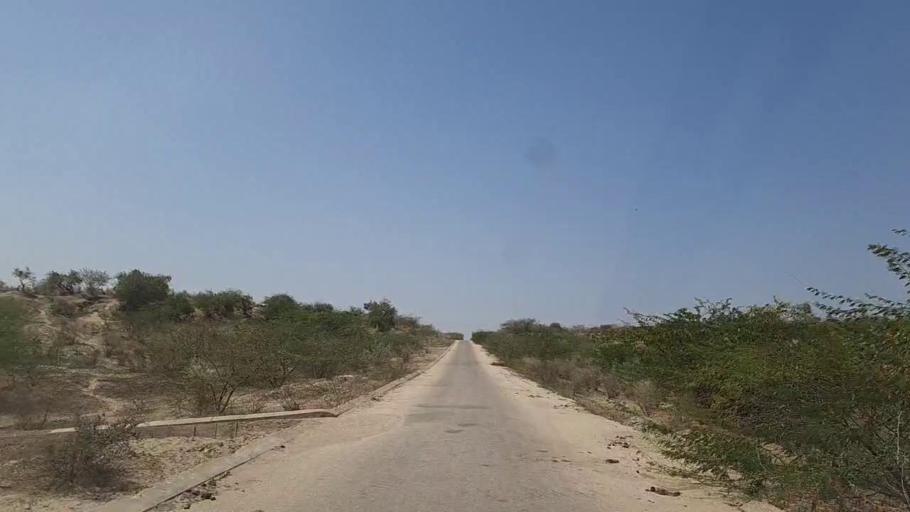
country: PK
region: Sindh
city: Diplo
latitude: 24.5217
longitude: 69.3581
